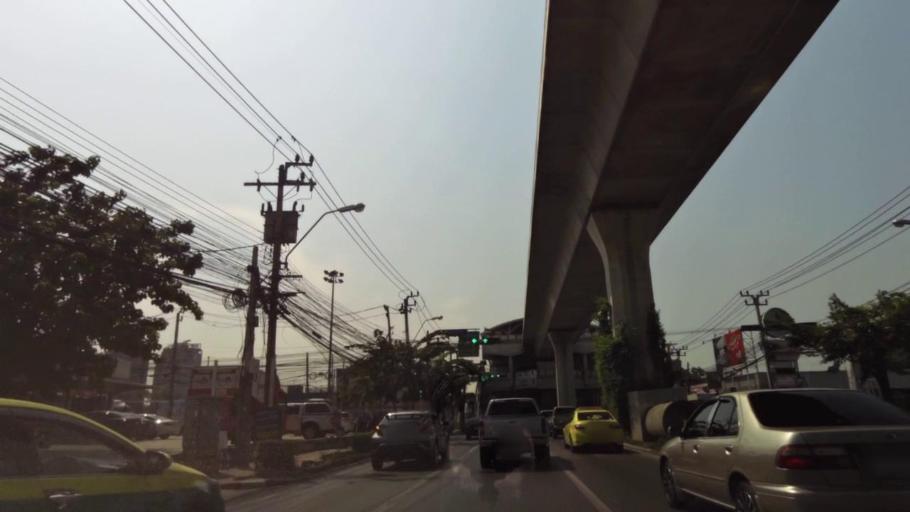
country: TH
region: Bangkok
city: Phra Khanong
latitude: 13.6626
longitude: 100.6025
